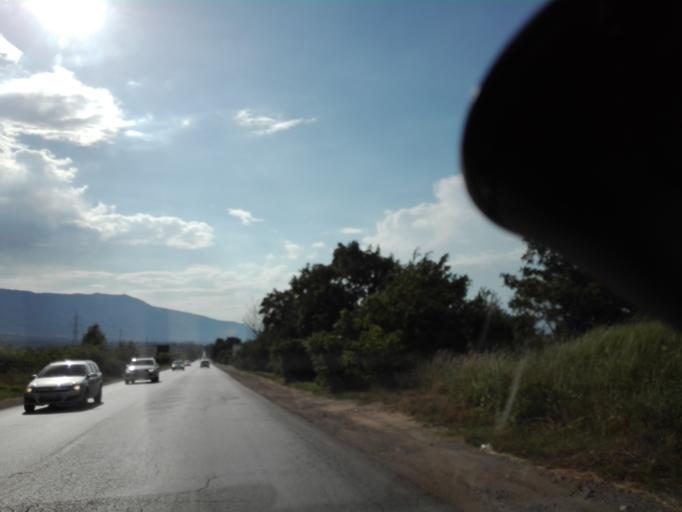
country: BG
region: Sofia-Capital
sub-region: Stolichna Obshtina
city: Sofia
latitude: 42.6215
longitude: 23.4310
